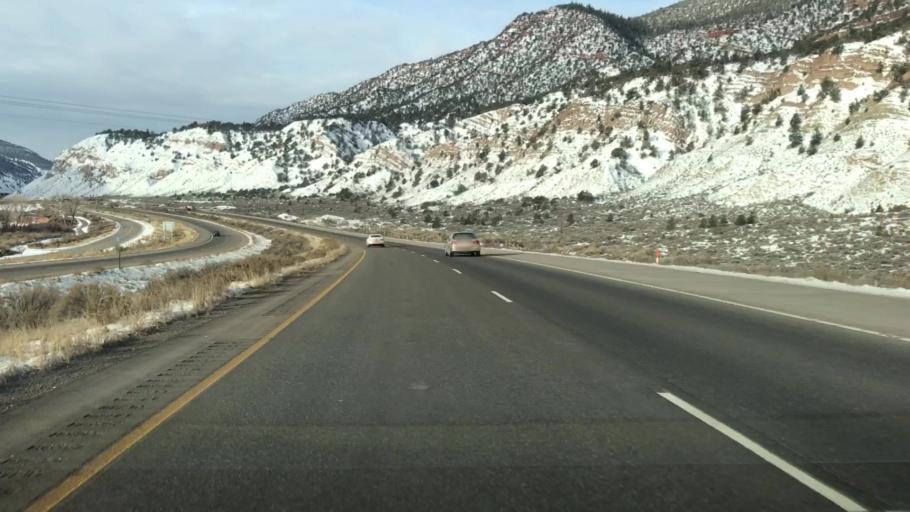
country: US
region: Colorado
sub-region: Eagle County
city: Gypsum
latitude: 39.6564
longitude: -106.9738
